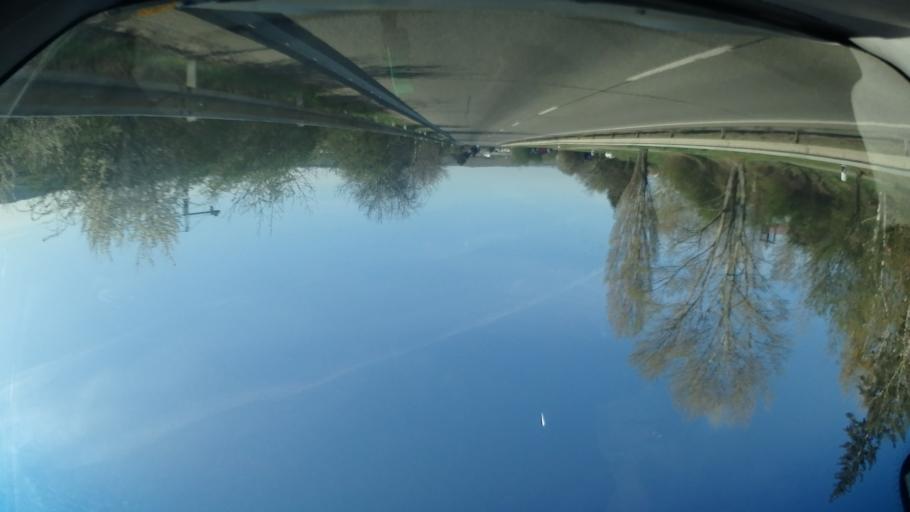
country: CZ
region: South Moravian
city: Ostopovice
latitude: 49.1762
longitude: 16.5476
